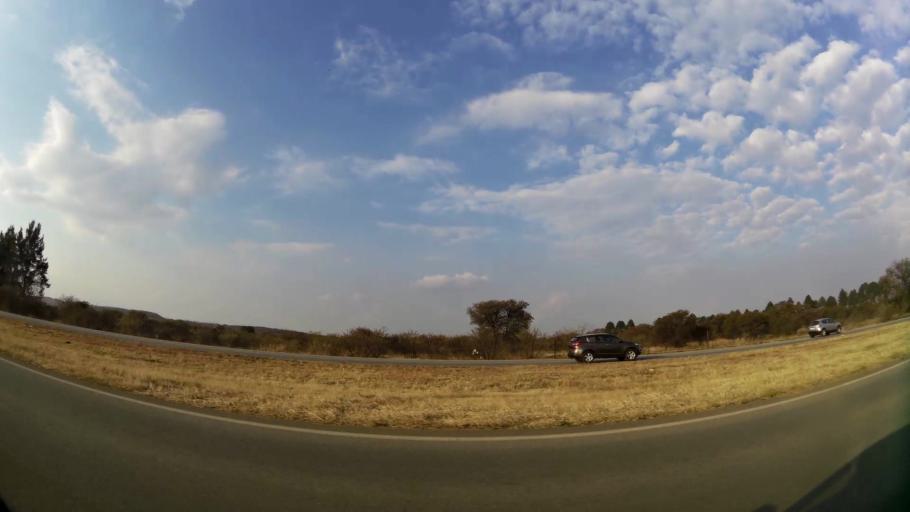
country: ZA
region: Gauteng
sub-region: Sedibeng District Municipality
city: Vereeniging
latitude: -26.6277
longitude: 27.8662
